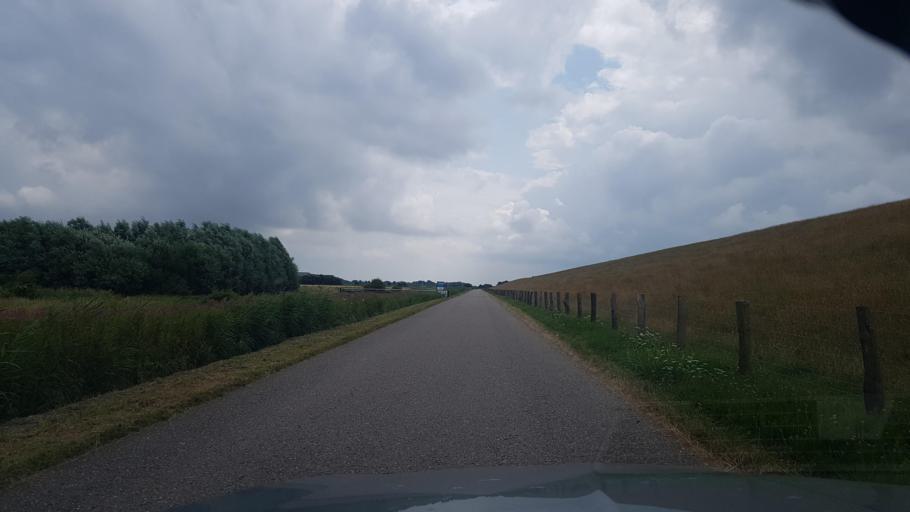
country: DE
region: Schleswig-Holstein
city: Elisabeth-Sophien-Koog
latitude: 54.4899
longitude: 8.8119
